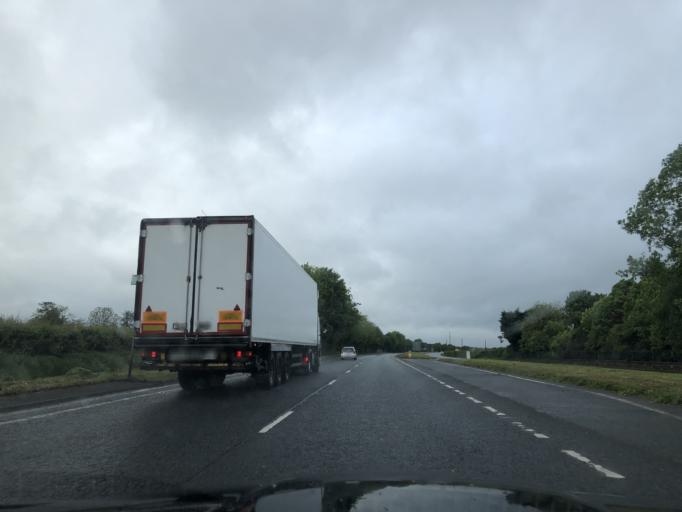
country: GB
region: Northern Ireland
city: Randalstown
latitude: 54.7510
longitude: -6.2384
